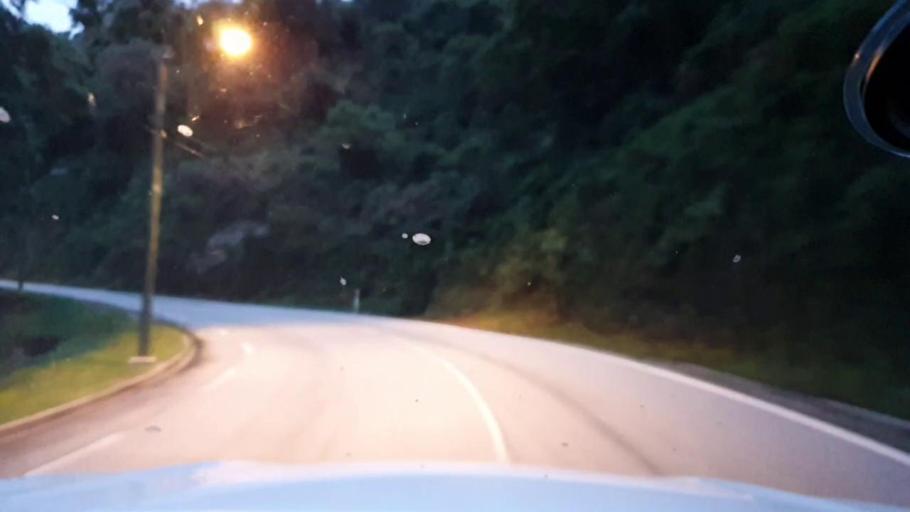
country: RW
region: Southern Province
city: Nzega
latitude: -2.5280
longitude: 29.3756
